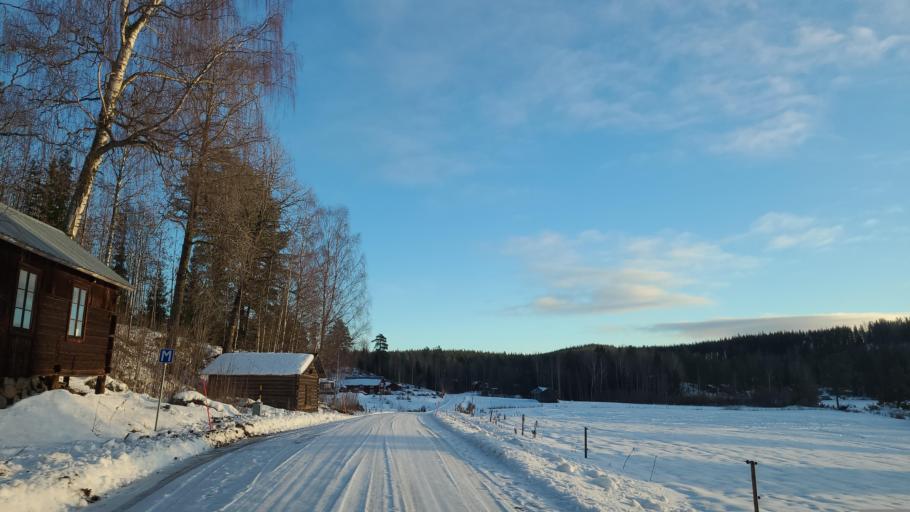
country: SE
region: Gaevleborg
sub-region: Bollnas Kommun
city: Kilafors
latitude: 61.3954
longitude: 16.6830
